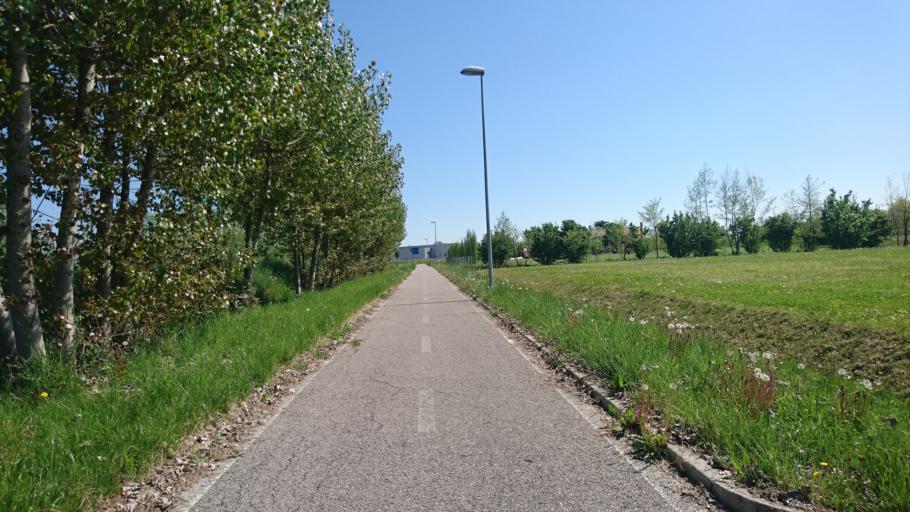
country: IT
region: Veneto
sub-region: Provincia di Treviso
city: Conscio
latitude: 45.6043
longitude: 12.2855
